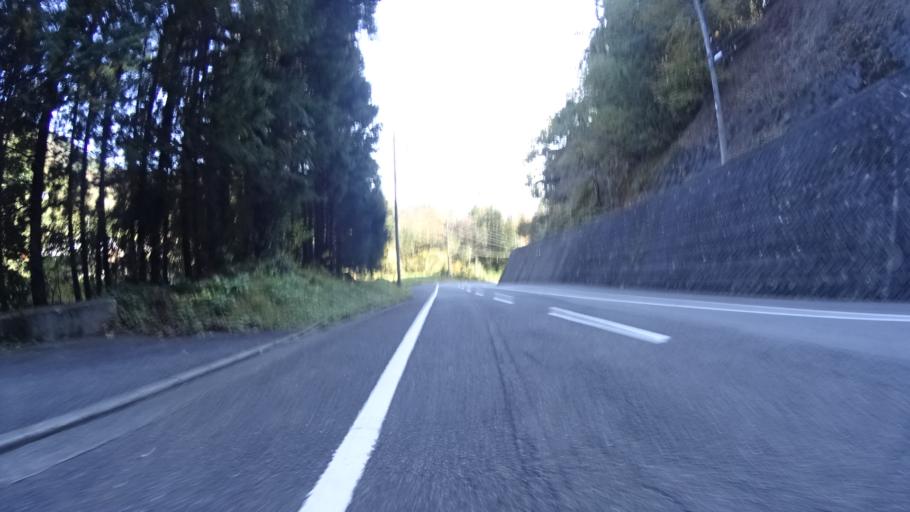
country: JP
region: Yamanashi
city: Uenohara
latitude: 35.6588
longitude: 139.1193
